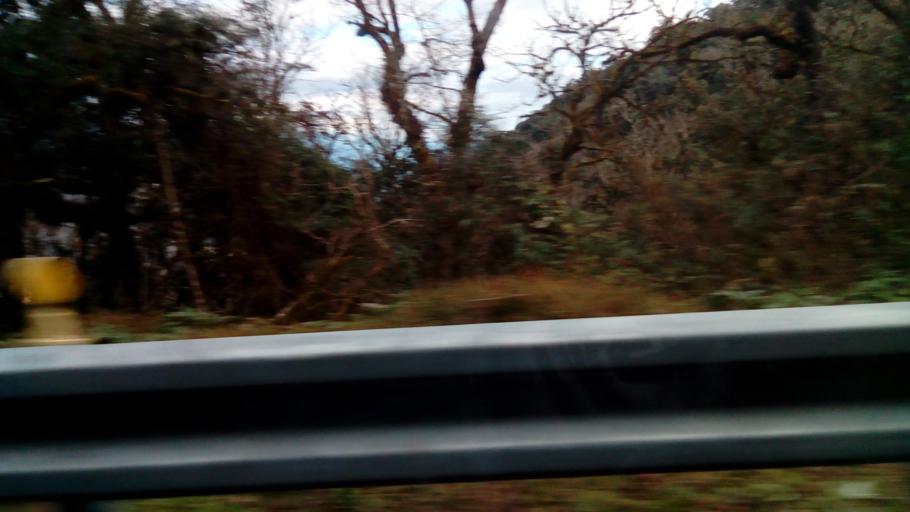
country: TW
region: Taiwan
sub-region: Hualien
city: Hualian
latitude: 24.3991
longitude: 121.3663
